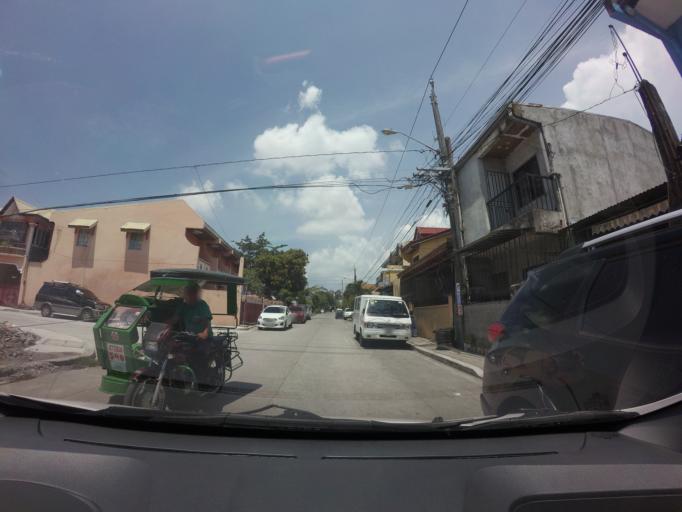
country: PH
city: Sambayanihan People's Village
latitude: 14.4225
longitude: 121.0098
